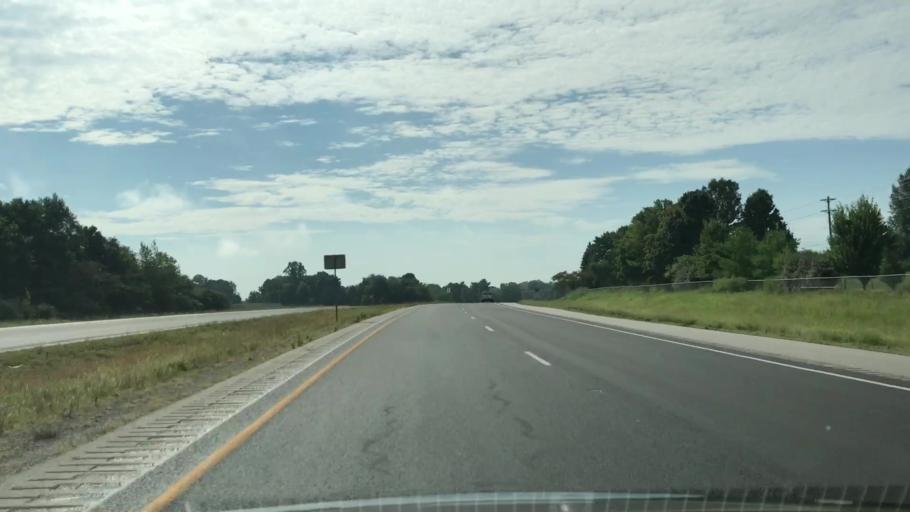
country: US
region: Kentucky
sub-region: Warren County
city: Plano
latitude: 36.8794
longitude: -86.3578
